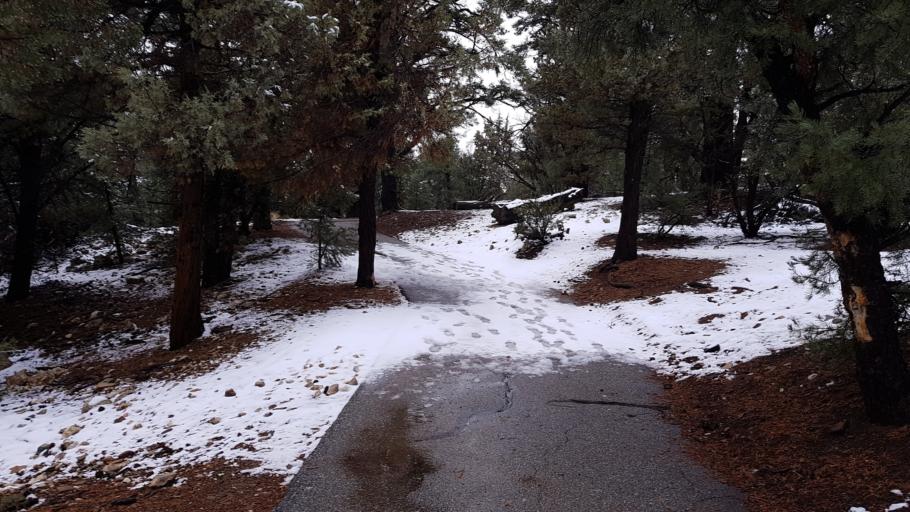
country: US
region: California
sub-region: San Bernardino County
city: Big Bear Lake
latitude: 34.2639
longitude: -116.9093
